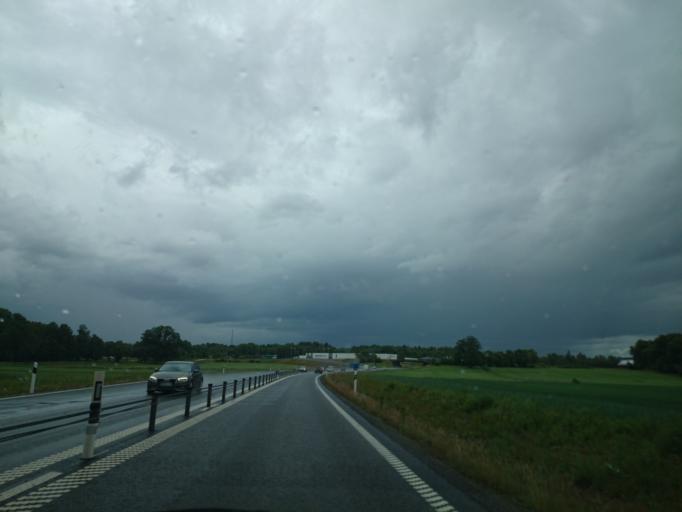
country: SE
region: Joenkoeping
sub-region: Varnamo Kommun
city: Varnamo
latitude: 57.1684
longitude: 14.0544
